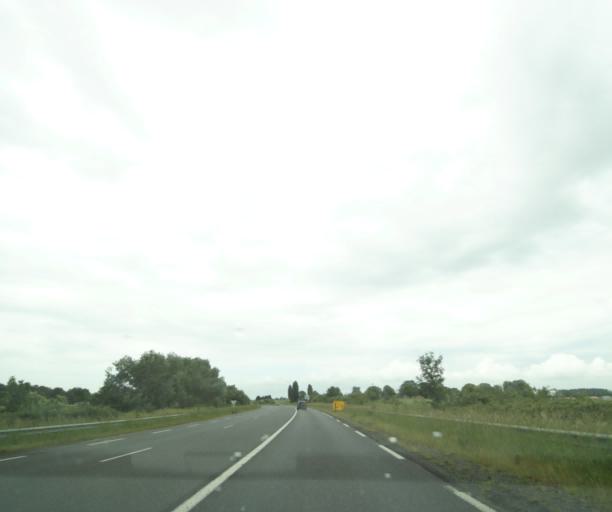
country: FR
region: Poitou-Charentes
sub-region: Departement des Deux-Sevres
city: Airvault
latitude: 46.8222
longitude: -0.2042
